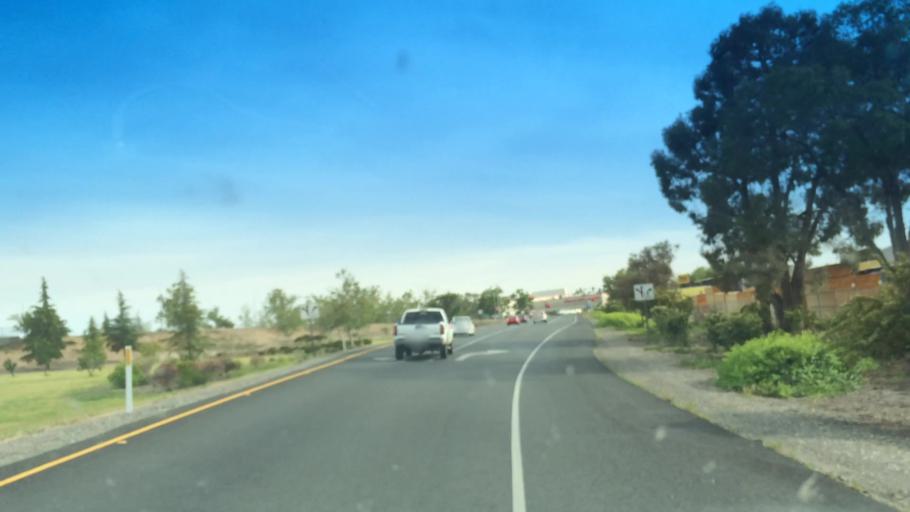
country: US
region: California
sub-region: Butte County
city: Chico
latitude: 39.7275
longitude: -121.8111
